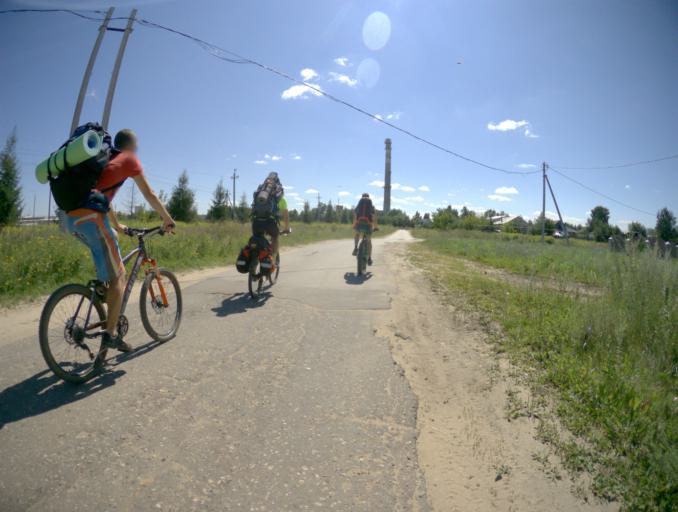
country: RU
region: Nizjnij Novgorod
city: Bor
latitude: 56.3771
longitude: 44.0509
